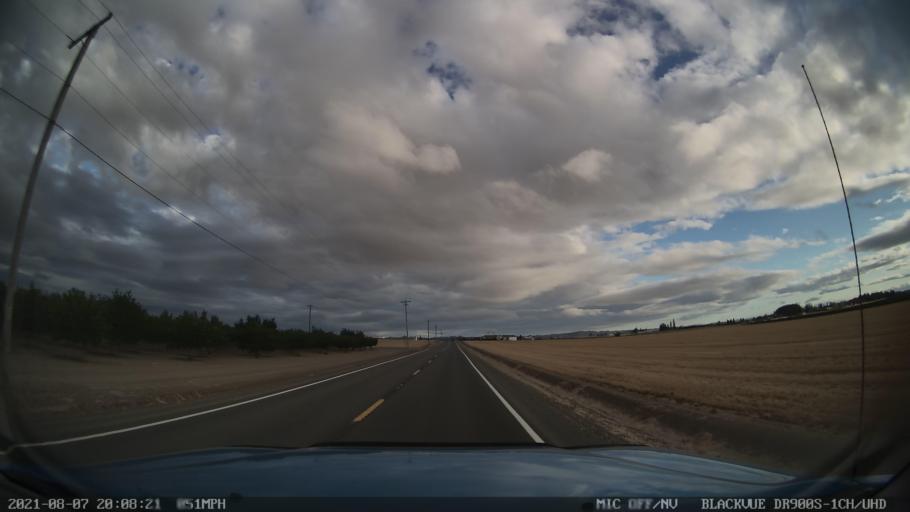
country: US
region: Oregon
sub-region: Marion County
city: Silverton
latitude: 44.9818
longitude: -122.8805
